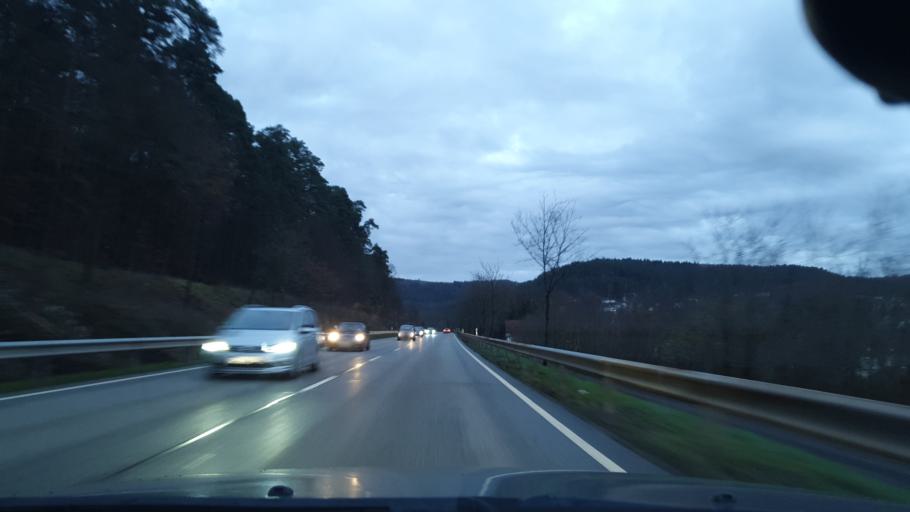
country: DE
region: Rheinland-Pfalz
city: Waldfischbach-Burgalben
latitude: 49.2877
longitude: 7.6489
